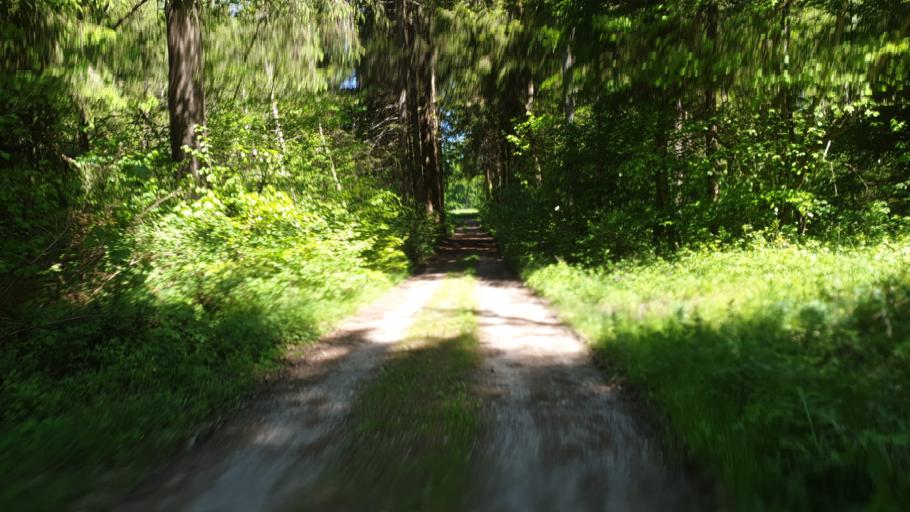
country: DE
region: Bavaria
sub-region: Upper Bavaria
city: Antdorf
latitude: 47.7654
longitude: 11.2927
